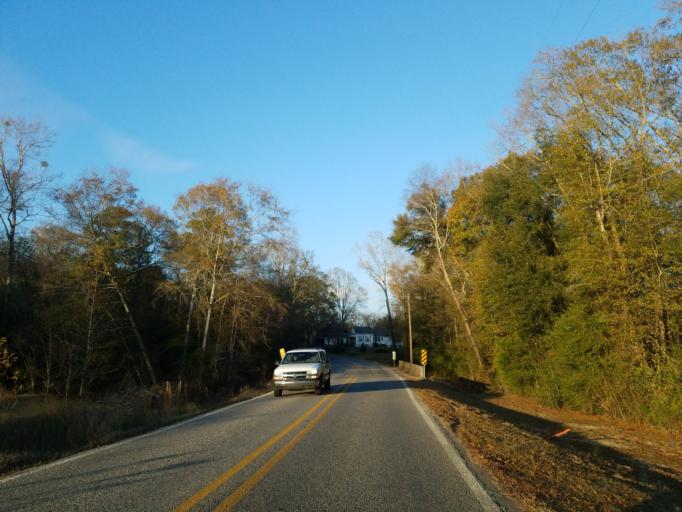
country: US
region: Mississippi
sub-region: Clarke County
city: Stonewall
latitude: 32.1762
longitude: -88.8289
